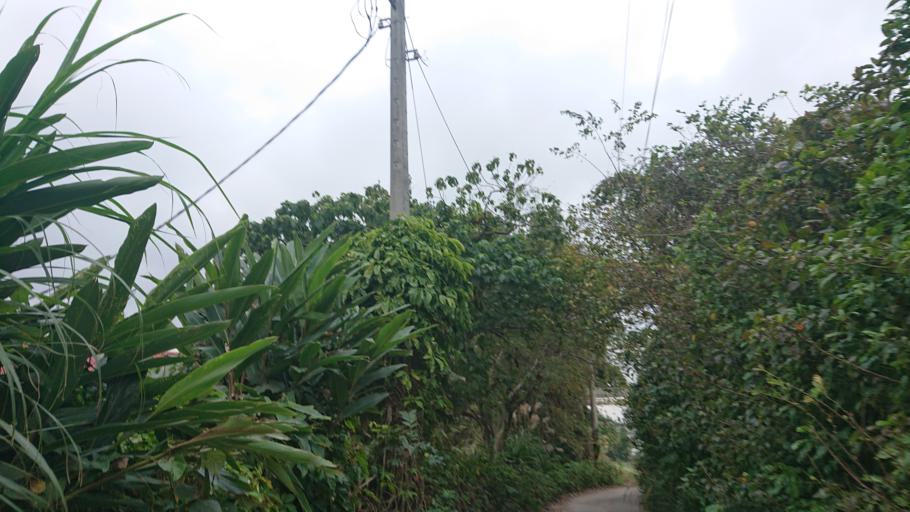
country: TW
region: Taiwan
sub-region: Taoyuan
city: Taoyuan
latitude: 24.9491
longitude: 121.3644
